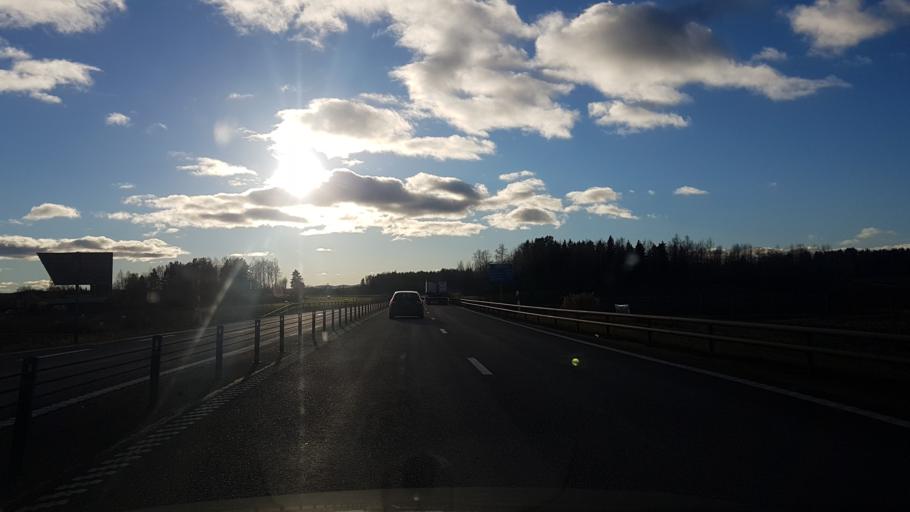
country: SE
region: Gaevleborg
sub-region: Sandvikens Kommun
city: Jarbo
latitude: 60.5996
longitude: 16.5822
